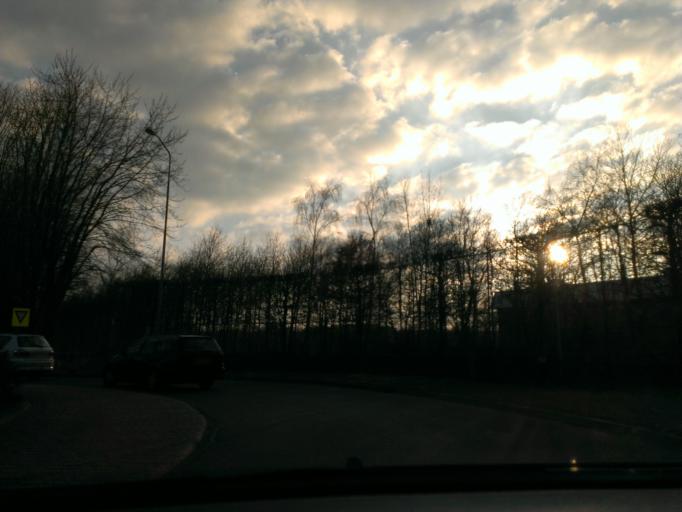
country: NL
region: Gelderland
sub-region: Gemeente Hattem
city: Hattem
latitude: 52.4691
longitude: 6.0696
